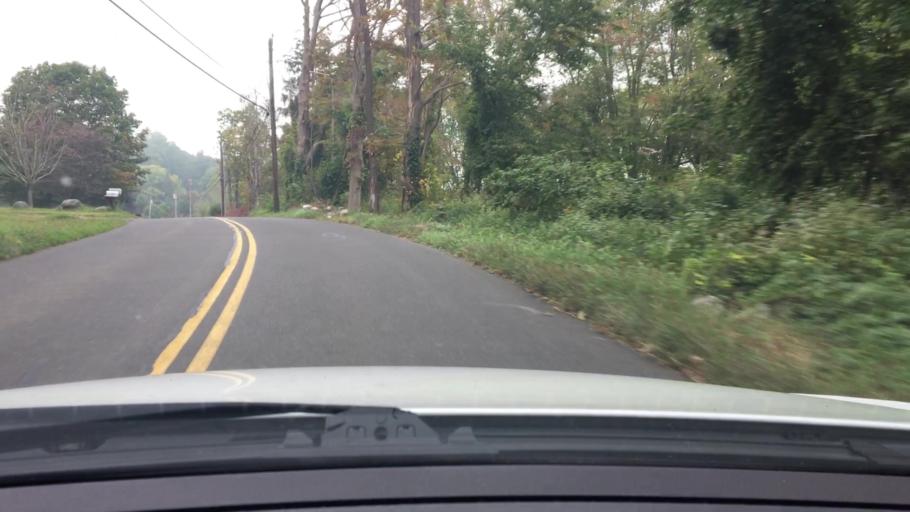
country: US
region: Connecticut
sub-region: Fairfield County
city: Newtown
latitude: 41.4568
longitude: -73.3567
